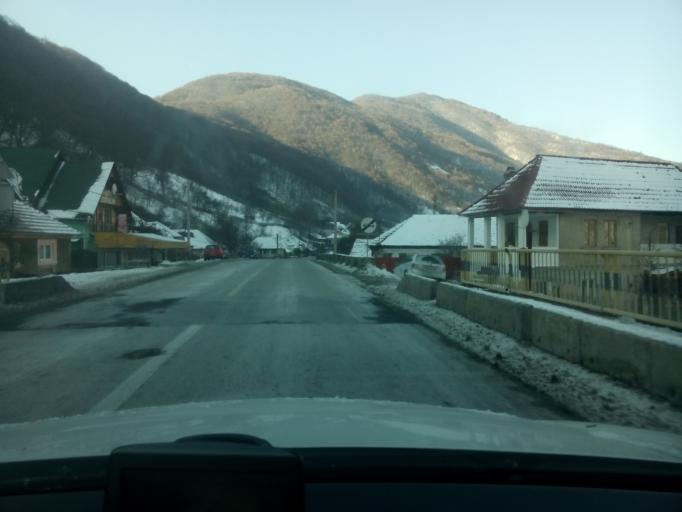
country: RO
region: Valcea
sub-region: Comuna Caineni
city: Greblesti
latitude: 45.4515
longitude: 24.2960
